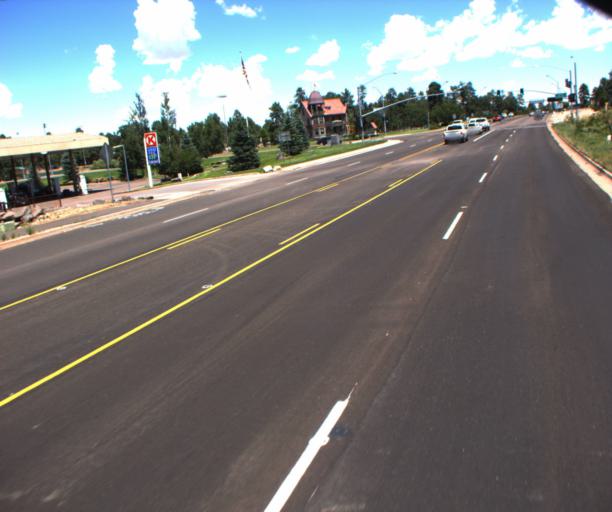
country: US
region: Arizona
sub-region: Navajo County
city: Show Low
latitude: 34.2403
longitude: -110.0595
